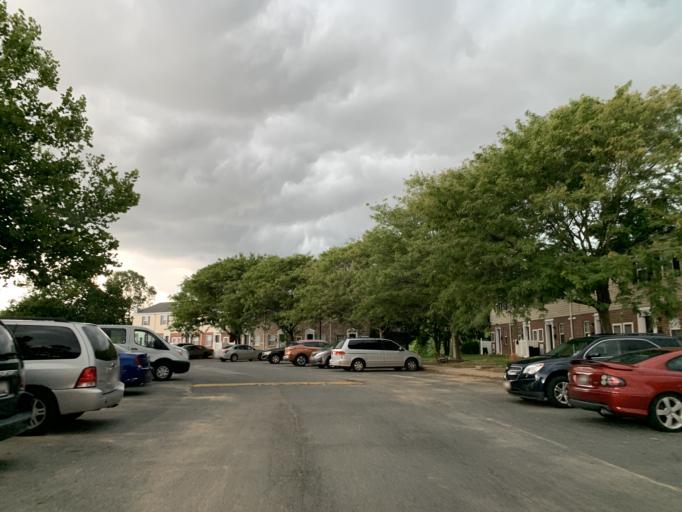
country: US
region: Maryland
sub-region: Baltimore County
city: Essex
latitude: 39.2994
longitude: -76.4552
